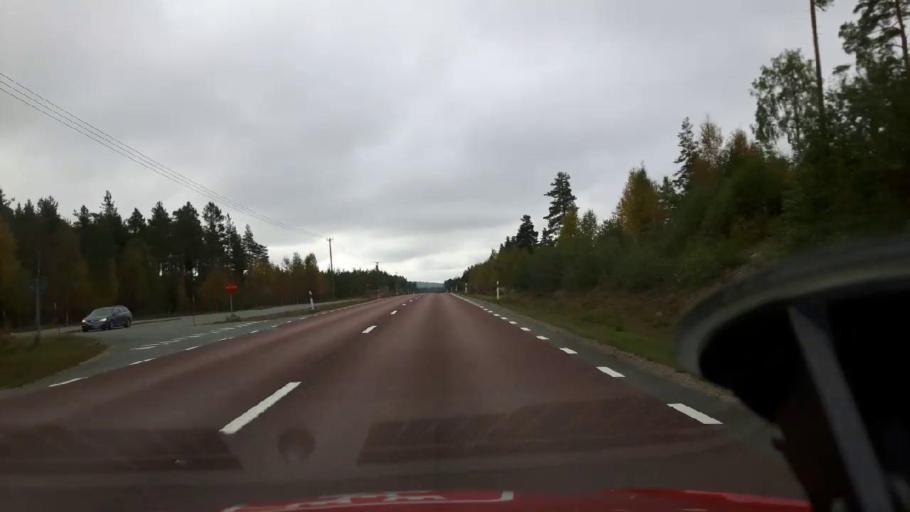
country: SE
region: Jaemtland
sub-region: Harjedalens Kommun
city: Sveg
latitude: 62.2405
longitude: 14.8306
